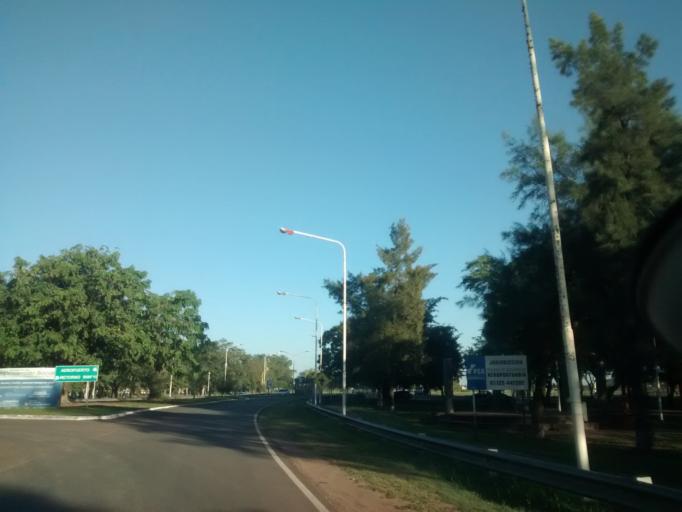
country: AR
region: Chaco
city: Fontana
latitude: -27.4443
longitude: -59.0243
